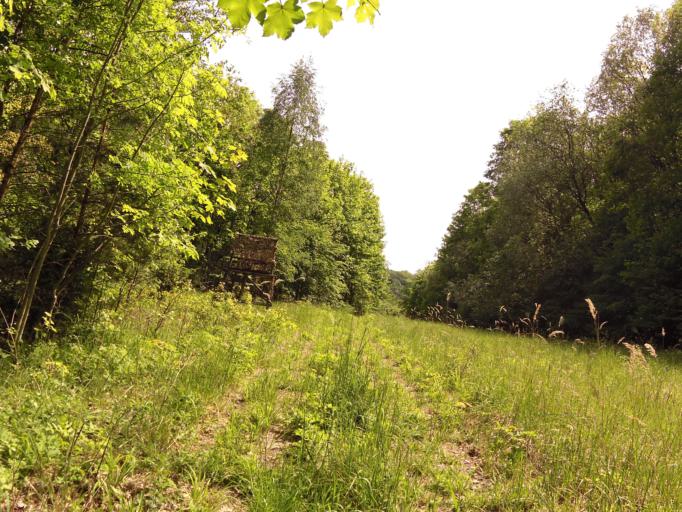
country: DE
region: Thuringia
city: Ifta
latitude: 51.0570
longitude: 10.1460
